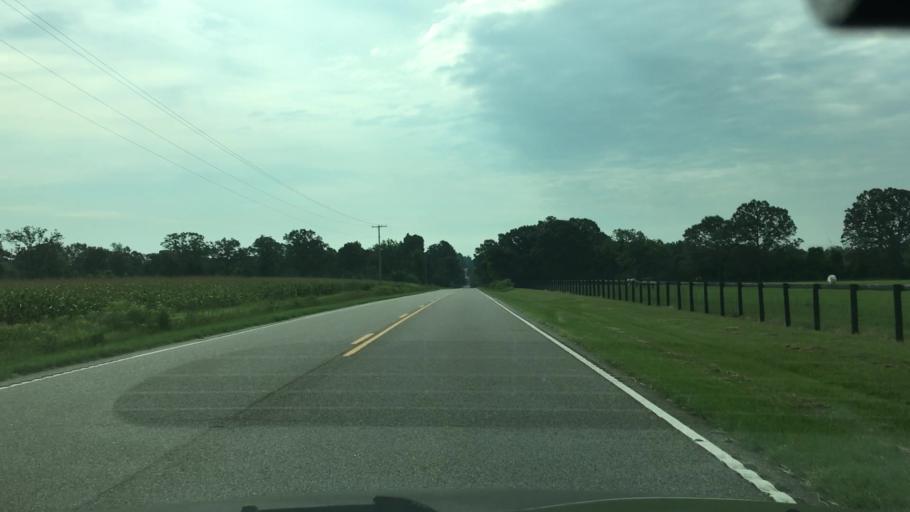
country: US
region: South Carolina
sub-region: Lexington County
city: Batesburg-Leesville
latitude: 33.6889
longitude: -81.4666
